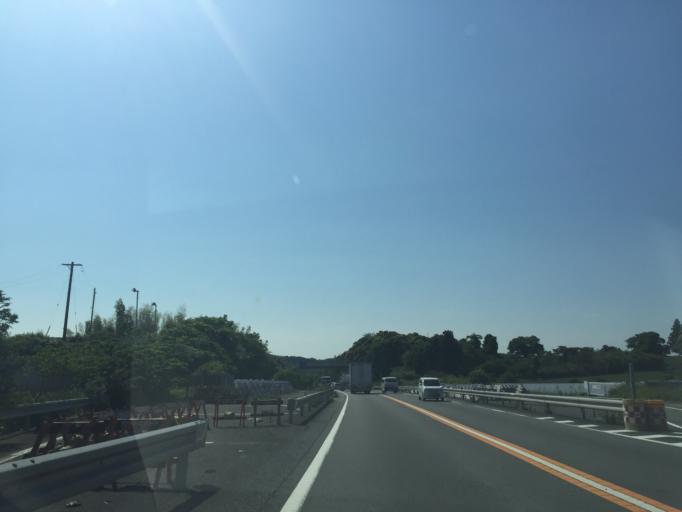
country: JP
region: Shizuoka
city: Kakegawa
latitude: 34.7874
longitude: 138.0207
